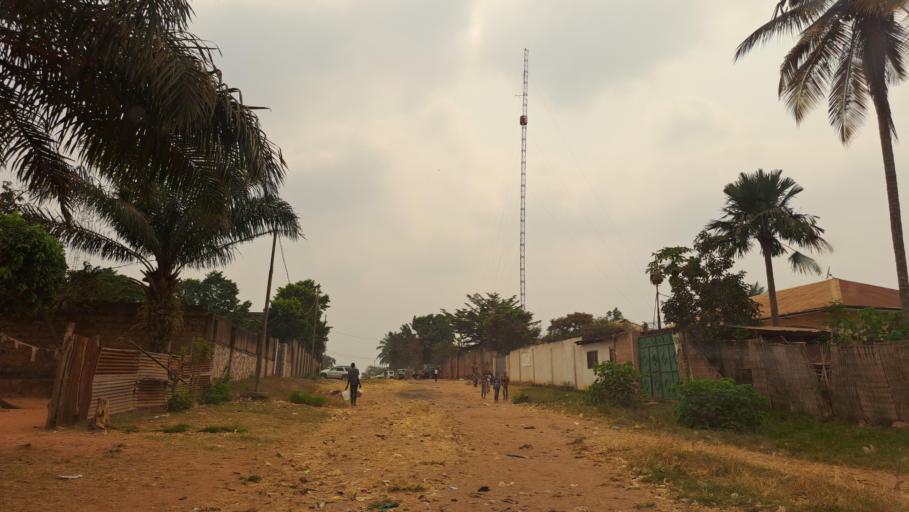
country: CD
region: Kasai-Oriental
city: Mbuji-Mayi
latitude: -6.1105
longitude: 23.5975
